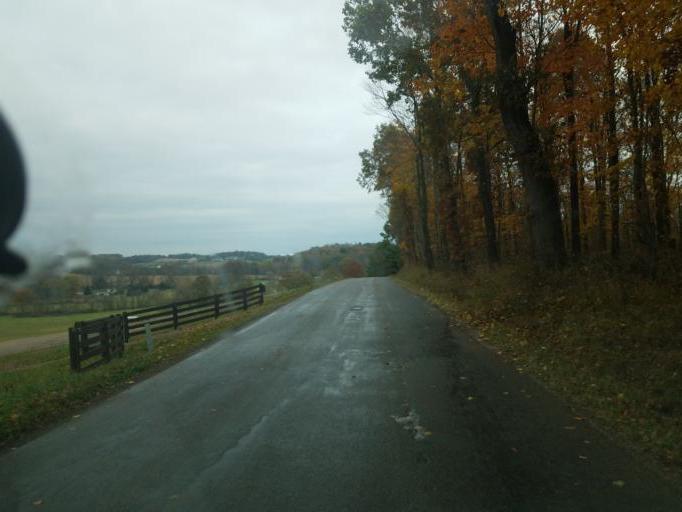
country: US
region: Ohio
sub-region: Knox County
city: Danville
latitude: 40.4909
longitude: -82.3609
